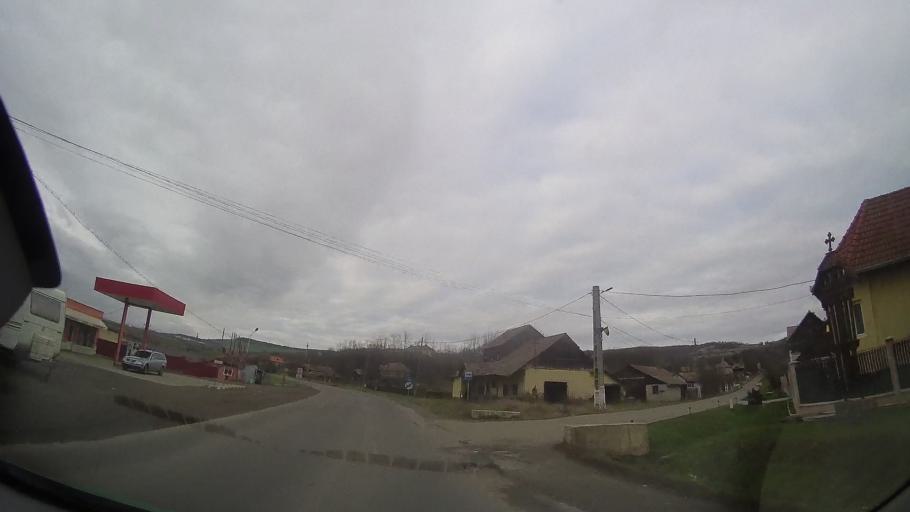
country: RO
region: Bistrita-Nasaud
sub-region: Comuna Urmenis
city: Urmenis
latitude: 46.7669
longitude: 24.3693
